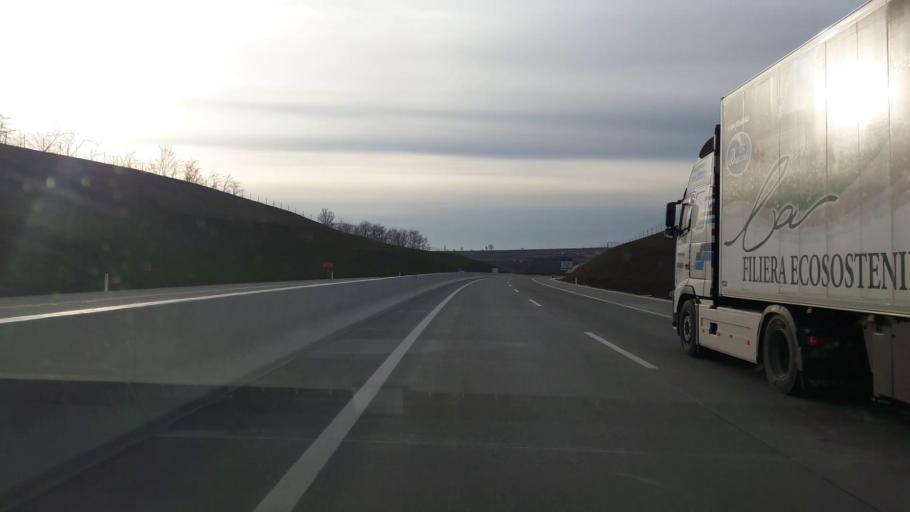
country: AT
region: Lower Austria
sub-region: Politischer Bezirk Mistelbach
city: Wilfersdorf
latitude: 48.6071
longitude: 16.6676
